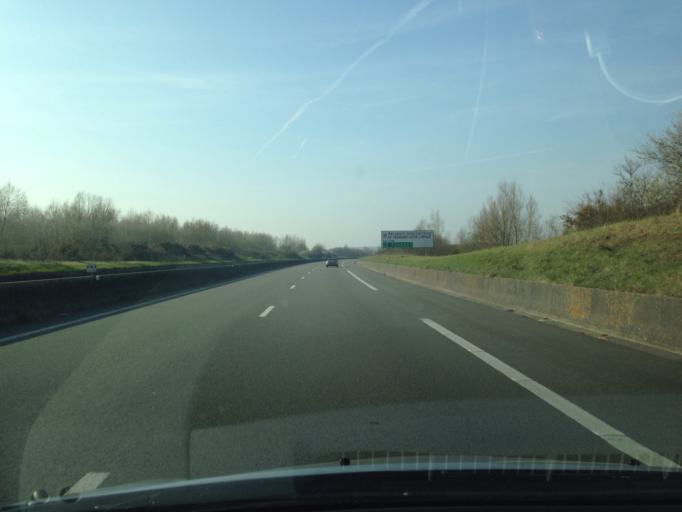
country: FR
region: Nord-Pas-de-Calais
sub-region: Departement du Pas-de-Calais
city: Saint-Josse
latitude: 50.4848
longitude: 1.6876
